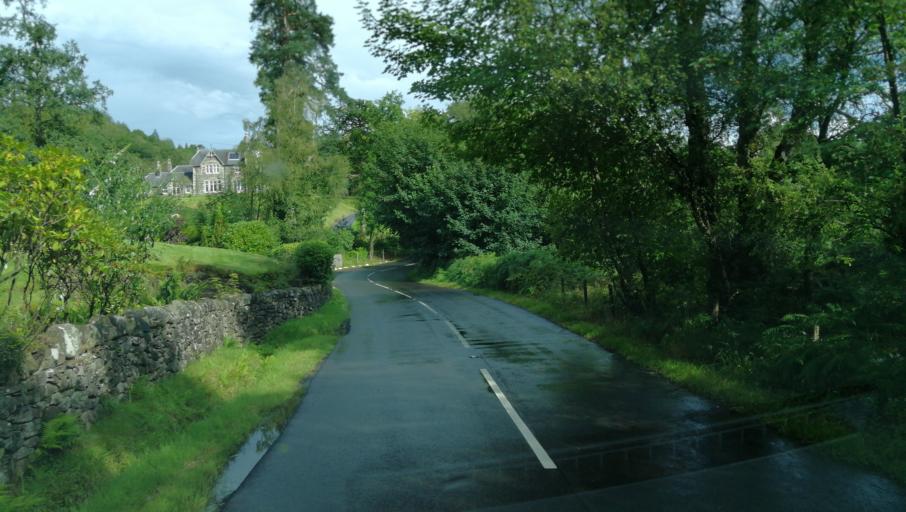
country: GB
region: Scotland
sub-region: Stirling
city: Balfron
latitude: 56.2297
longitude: -4.3946
